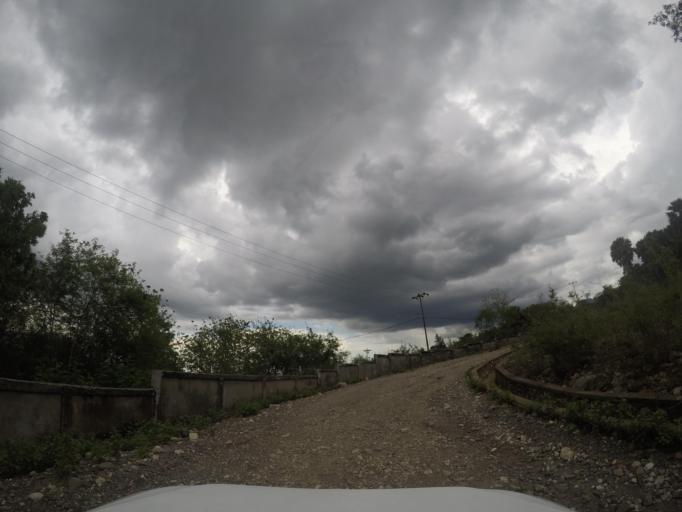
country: TL
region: Bobonaro
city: Maliana
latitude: -8.9737
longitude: 125.2259
